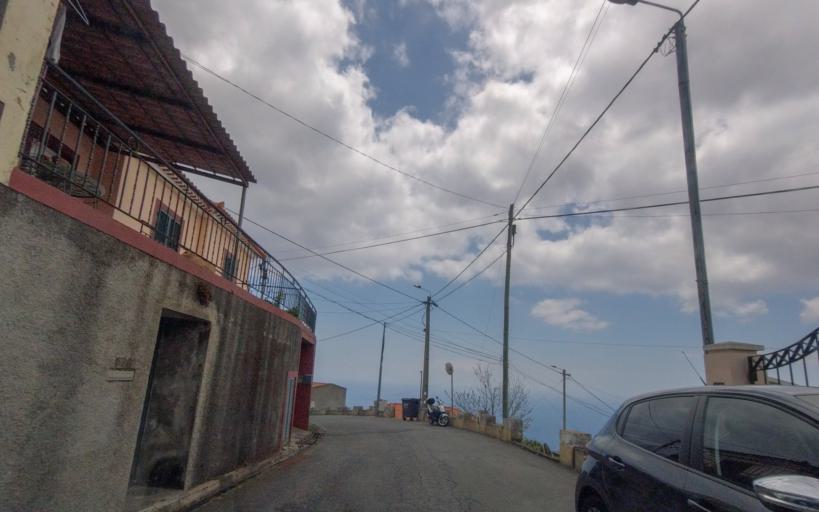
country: PT
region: Madeira
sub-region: Funchal
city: Nossa Senhora do Monte
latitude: 32.6659
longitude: -16.8801
